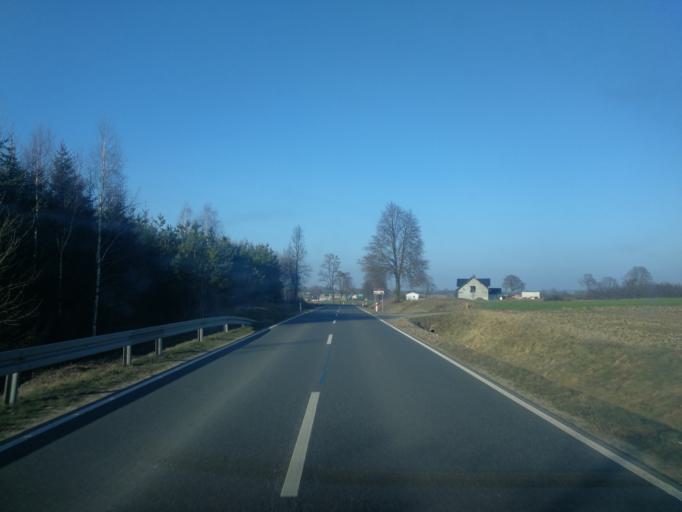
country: PL
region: Warmian-Masurian Voivodeship
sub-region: Powiat ilawski
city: Lubawa
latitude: 53.4484
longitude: 19.7774
